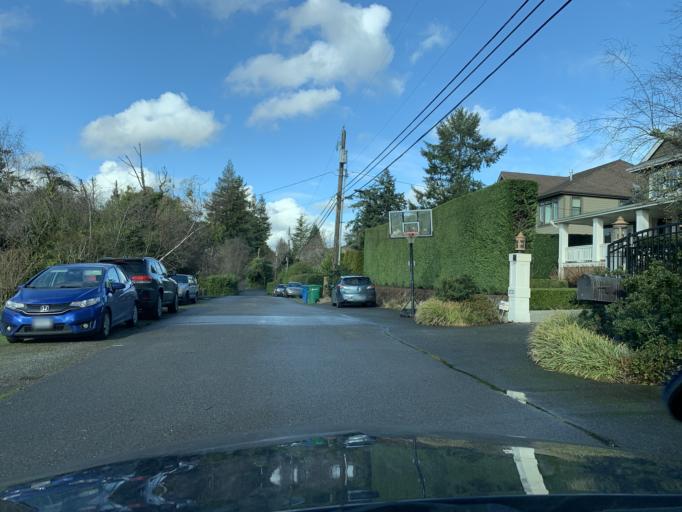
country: US
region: Washington
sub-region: King County
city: Mercer Island
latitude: 47.5860
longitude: -122.2515
